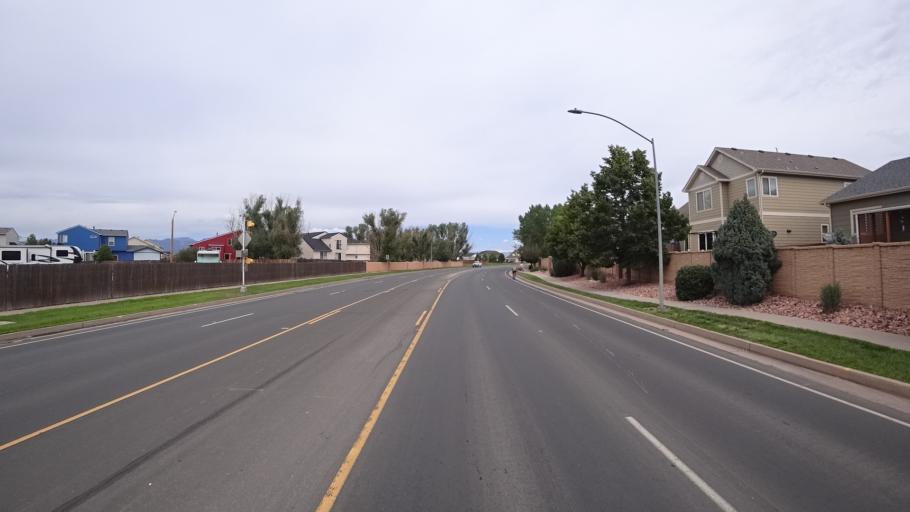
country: US
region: Colorado
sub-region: El Paso County
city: Fountain
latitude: 38.7127
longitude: -104.7003
